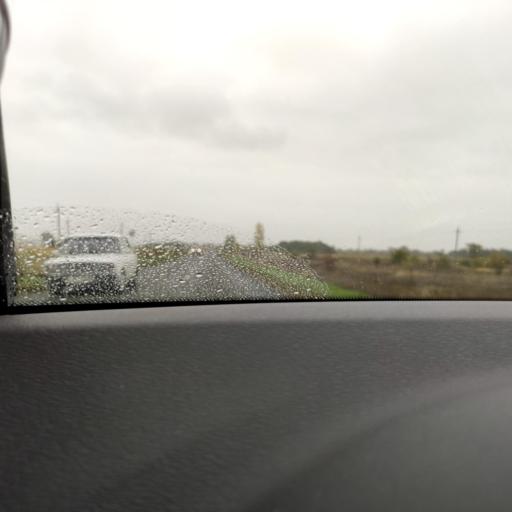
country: RU
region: Samara
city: Yelkhovka
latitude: 53.7395
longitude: 50.2802
